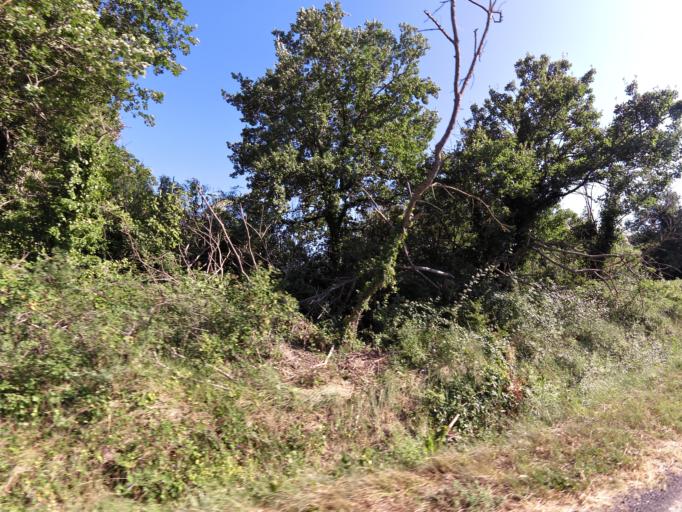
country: FR
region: Languedoc-Roussillon
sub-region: Departement de l'Herault
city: Boisseron
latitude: 43.7694
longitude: 4.0642
